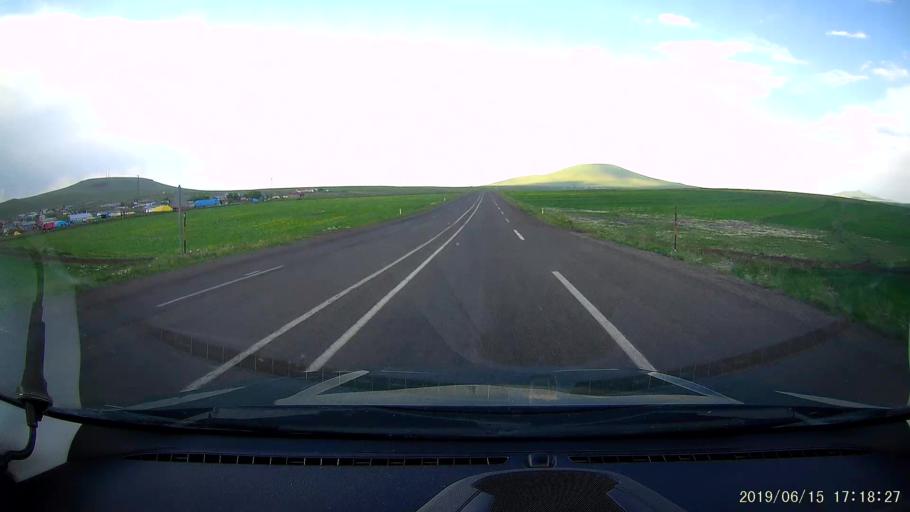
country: TR
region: Kars
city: Kars
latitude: 40.6130
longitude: 43.2580
